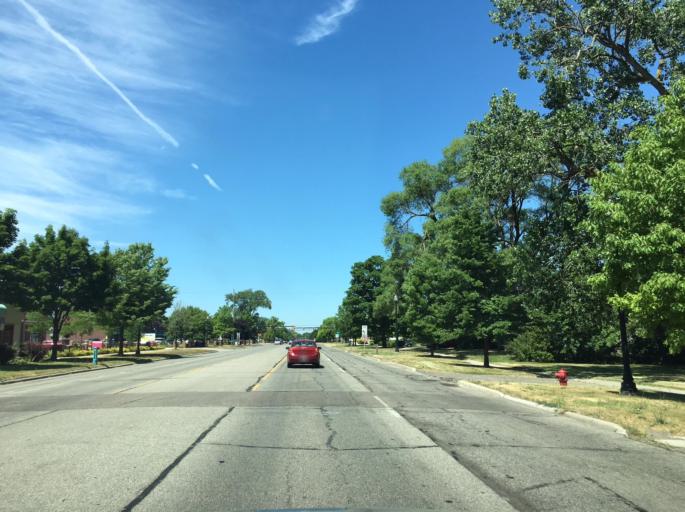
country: US
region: Michigan
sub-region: Wayne County
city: Taylor
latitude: 42.2271
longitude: -83.2518
